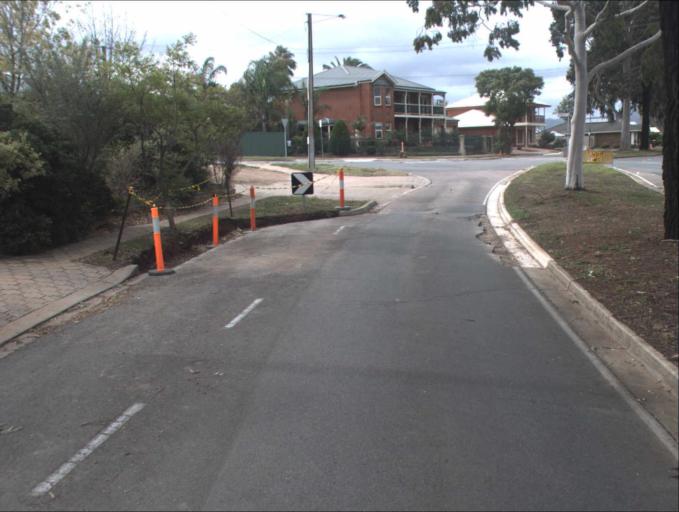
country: AU
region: South Australia
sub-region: Port Adelaide Enfield
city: Klemzig
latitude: -34.8709
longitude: 138.6508
